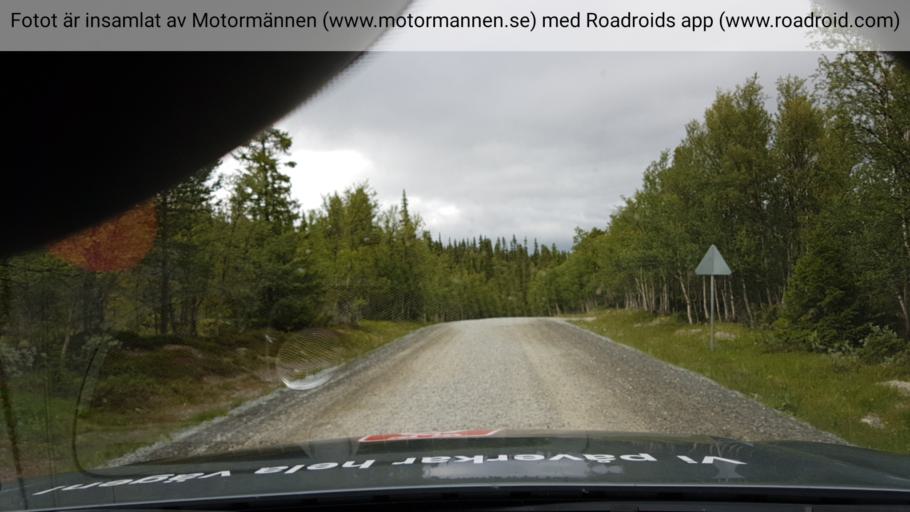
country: SE
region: Jaemtland
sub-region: Are Kommun
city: Are
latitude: 62.7941
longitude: 12.7623
